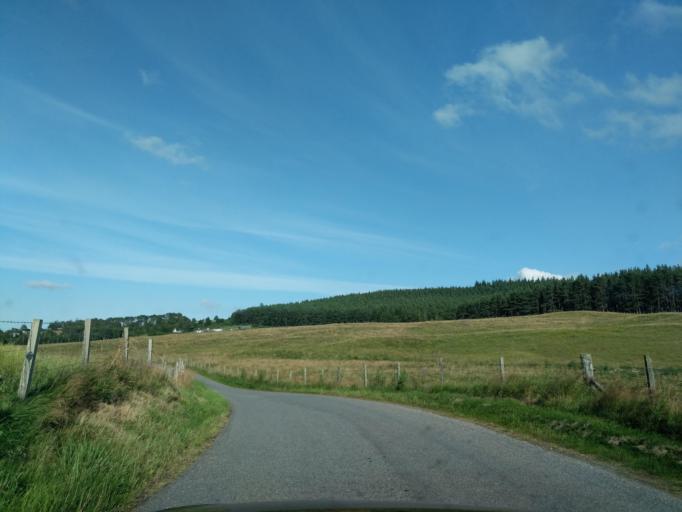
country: GB
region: Scotland
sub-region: Highland
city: Grantown on Spey
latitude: 57.2880
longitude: -3.7266
